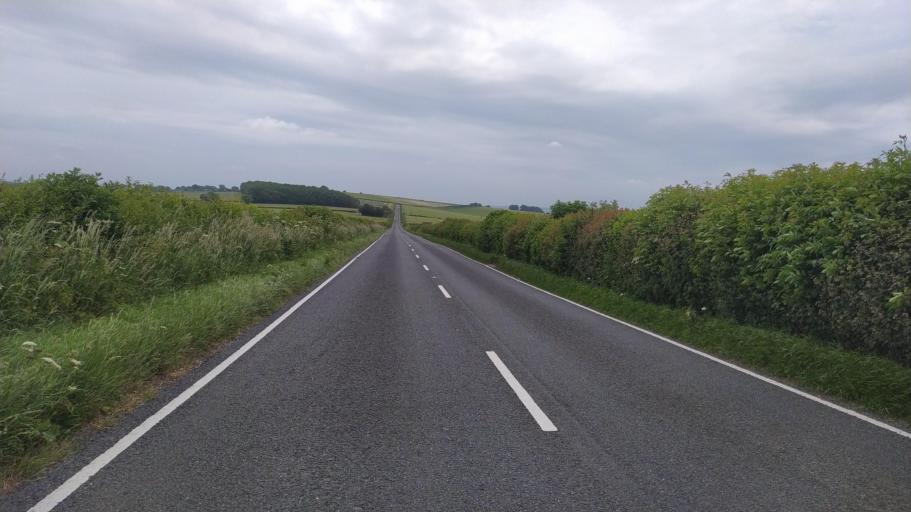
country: GB
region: England
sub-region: Dorset
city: Dorchester
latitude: 50.7741
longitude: -2.4536
